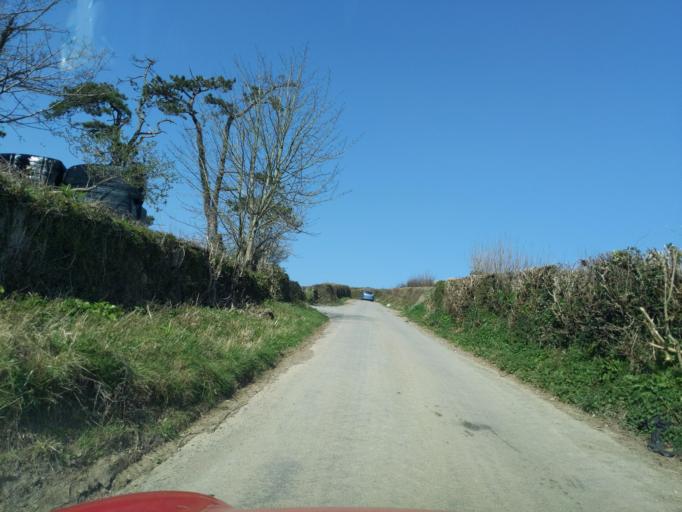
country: GB
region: England
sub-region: Devon
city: Bere Alston
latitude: 50.4463
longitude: -4.1504
